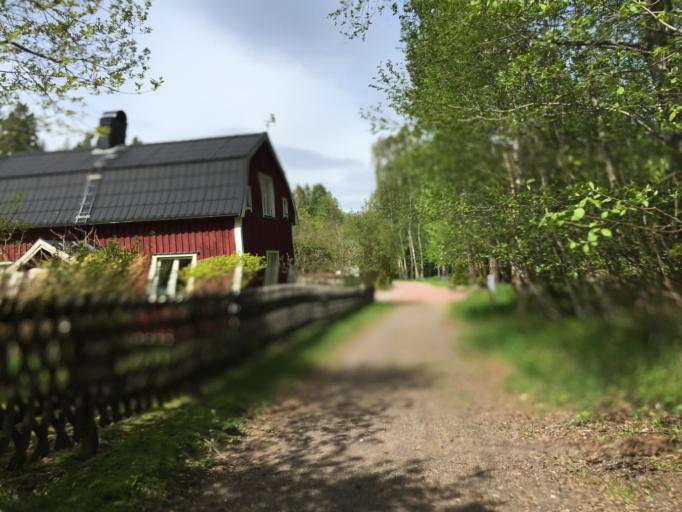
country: SE
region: Dalarna
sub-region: Ludvika Kommun
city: Ludvika
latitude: 60.1363
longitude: 15.1500
